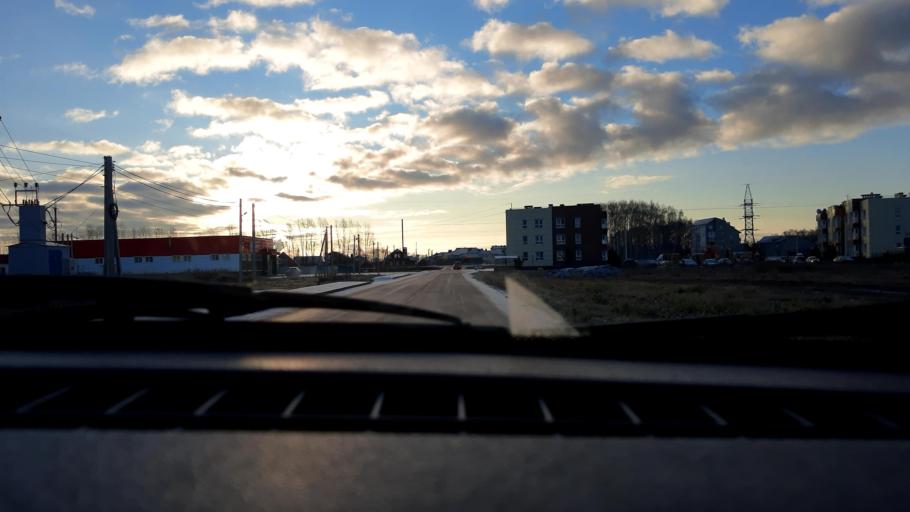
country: RU
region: Bashkortostan
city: Mikhaylovka
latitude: 54.7852
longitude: 55.8328
